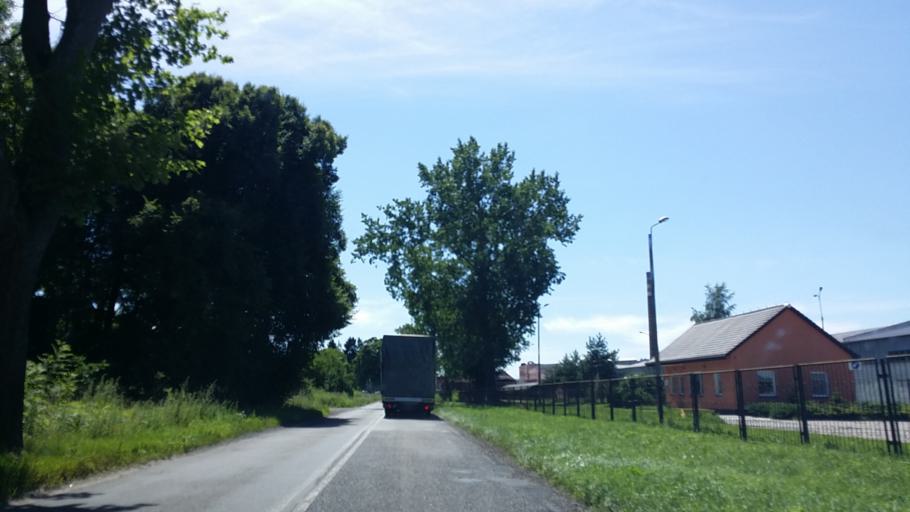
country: PL
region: West Pomeranian Voivodeship
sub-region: Powiat lobeski
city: Lobez
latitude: 53.6454
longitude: 15.6367
